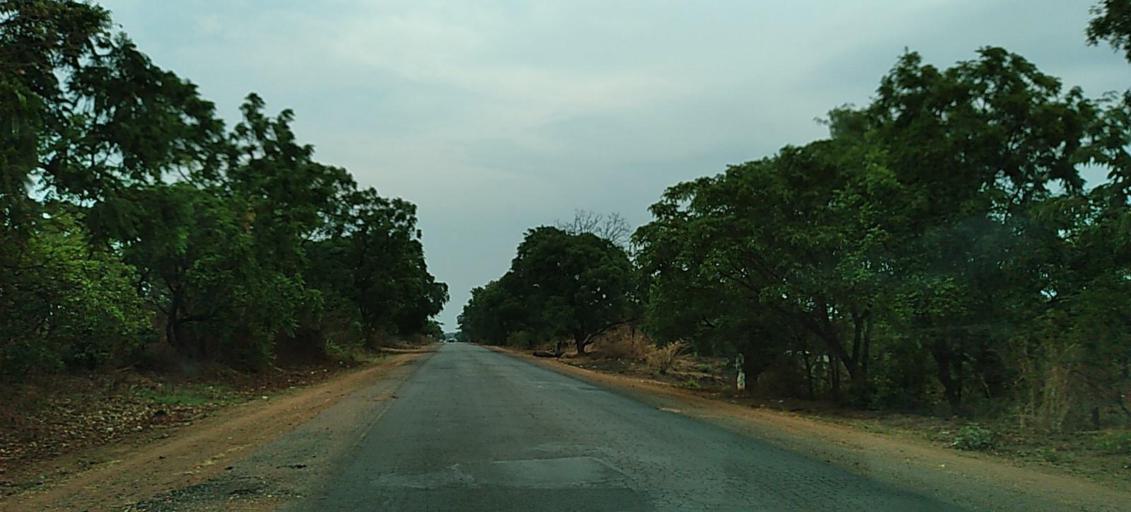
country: ZM
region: Copperbelt
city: Luanshya
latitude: -13.1024
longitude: 28.4292
